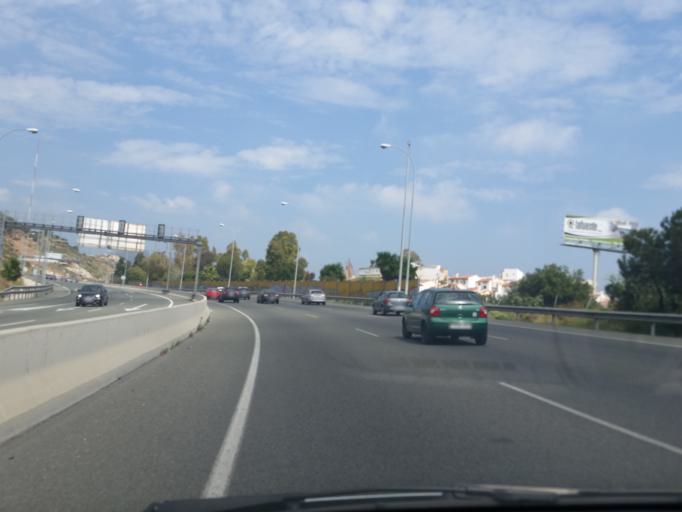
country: ES
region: Andalusia
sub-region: Provincia de Malaga
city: Malaga
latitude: 36.7264
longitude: -4.4536
